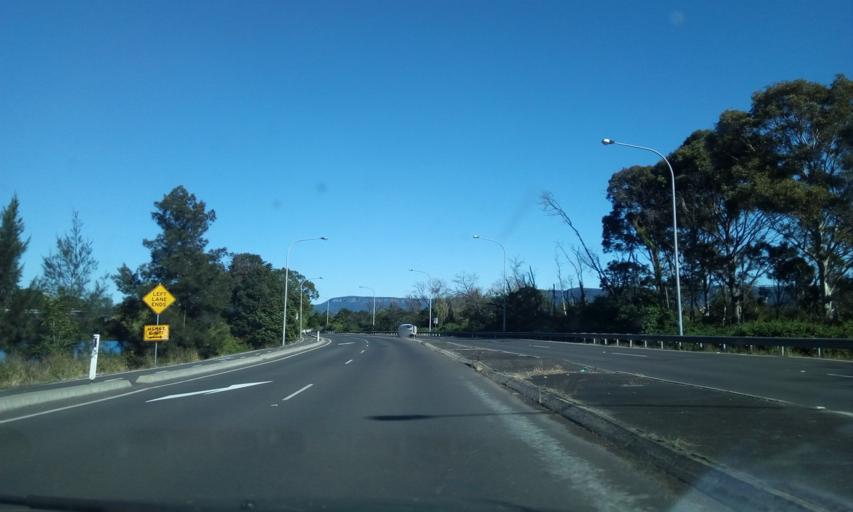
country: AU
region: New South Wales
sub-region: Wollongong
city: Koonawarra
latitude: -34.4748
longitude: 150.8111
